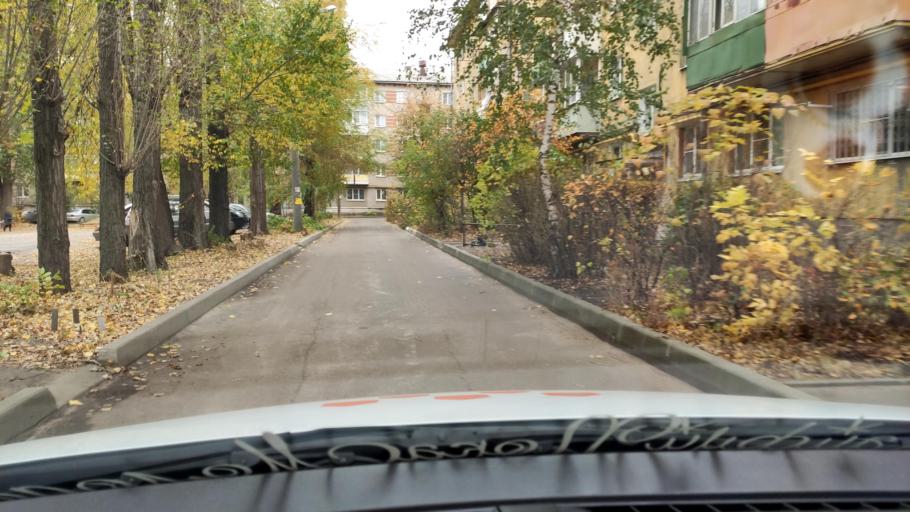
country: RU
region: Voronezj
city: Voronezh
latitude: 51.6695
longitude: 39.1485
